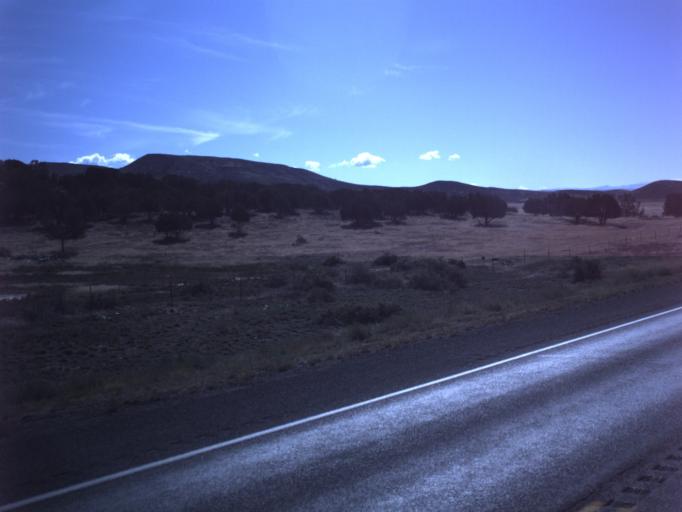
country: US
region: Utah
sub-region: Sanpete County
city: Gunnison
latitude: 39.2212
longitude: -111.8482
